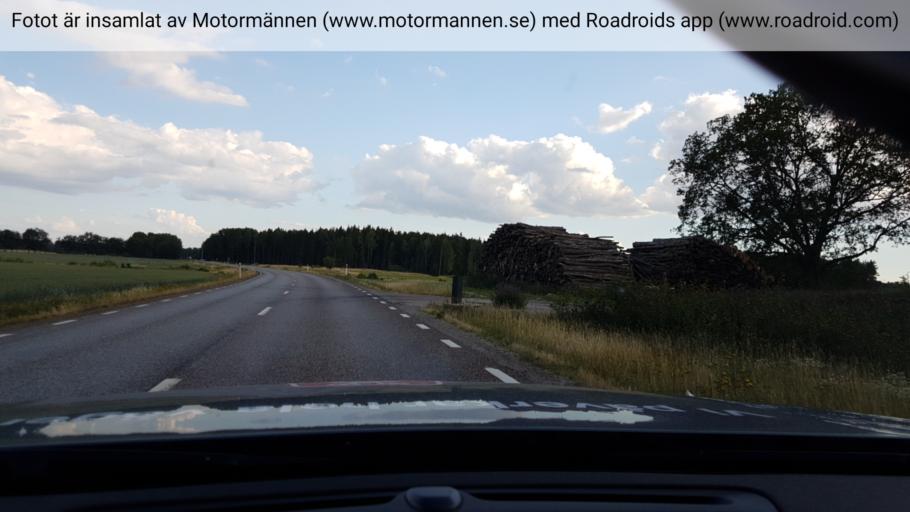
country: SE
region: Uppsala
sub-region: Enkopings Kommun
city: Irsta
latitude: 59.7990
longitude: 16.9014
